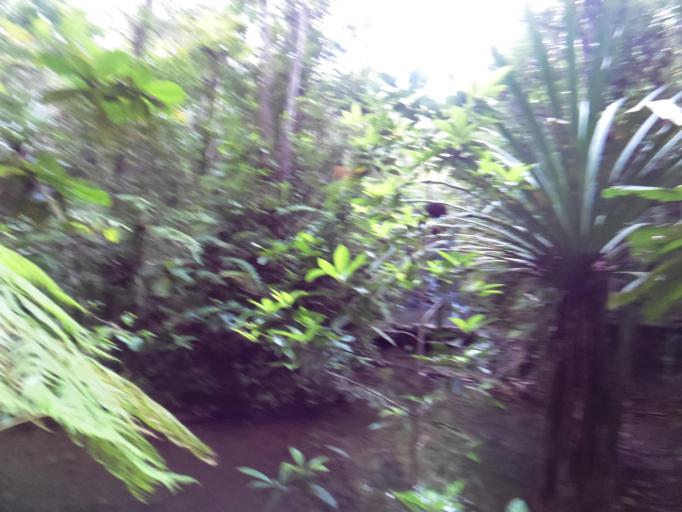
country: FJ
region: Central
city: Suva
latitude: -18.0596
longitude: 178.4705
